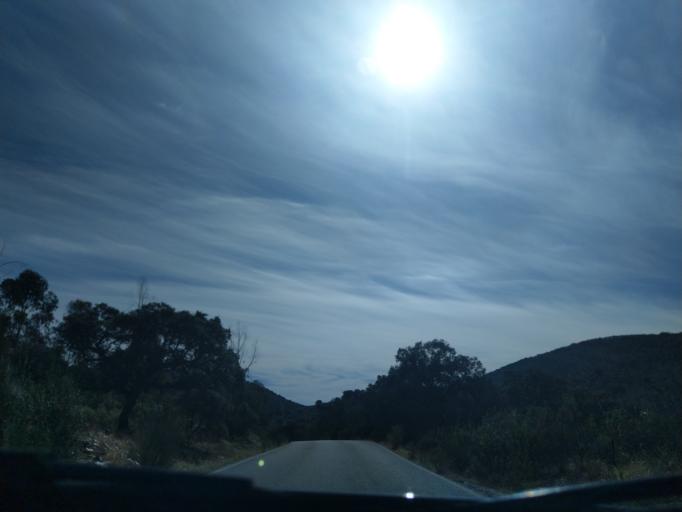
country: ES
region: Extremadura
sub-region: Provincia de Badajoz
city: Reina
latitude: 38.1293
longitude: -5.9152
